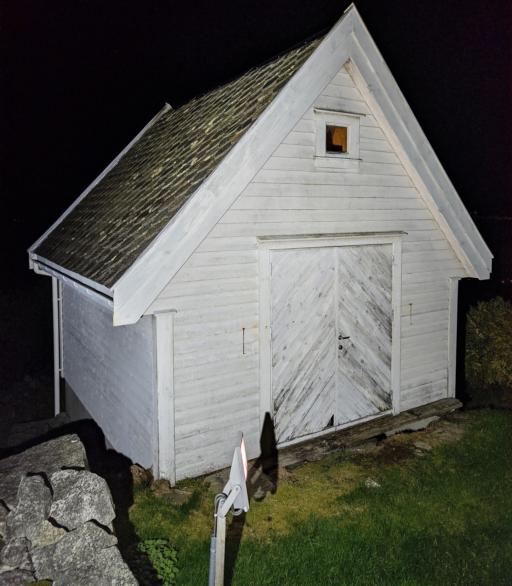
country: NO
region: Sogn og Fjordane
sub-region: Vik
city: Vikoyri
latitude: 61.1697
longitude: 6.6416
